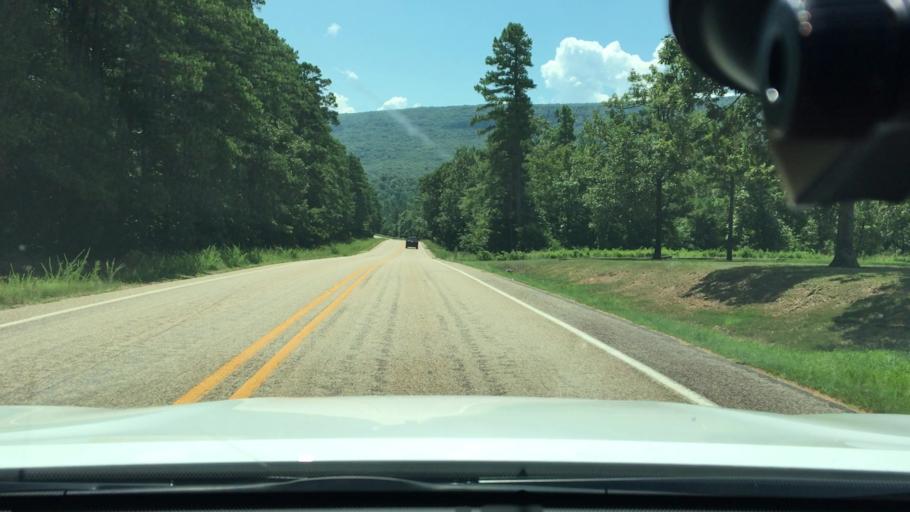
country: US
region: Arkansas
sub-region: Logan County
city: Paris
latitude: 35.1964
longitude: -93.6339
